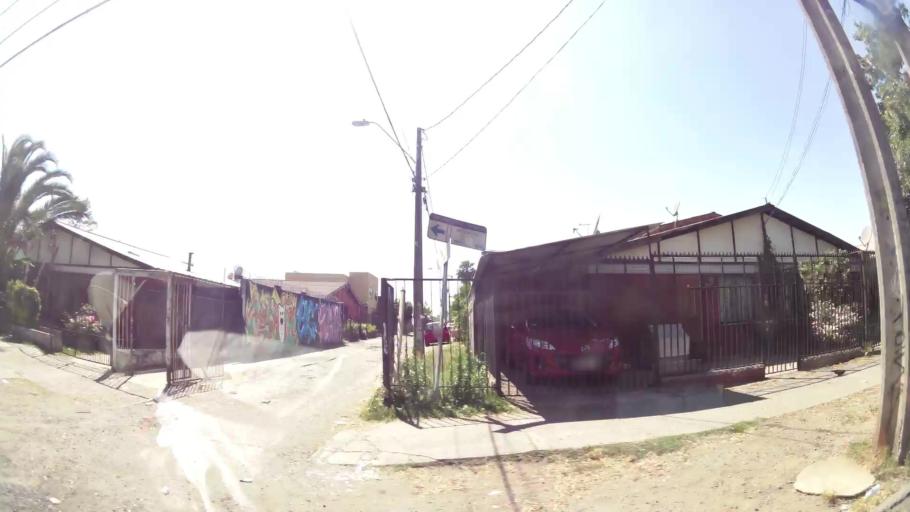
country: CL
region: Santiago Metropolitan
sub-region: Provincia de Santiago
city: La Pintana
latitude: -33.5617
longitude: -70.6566
